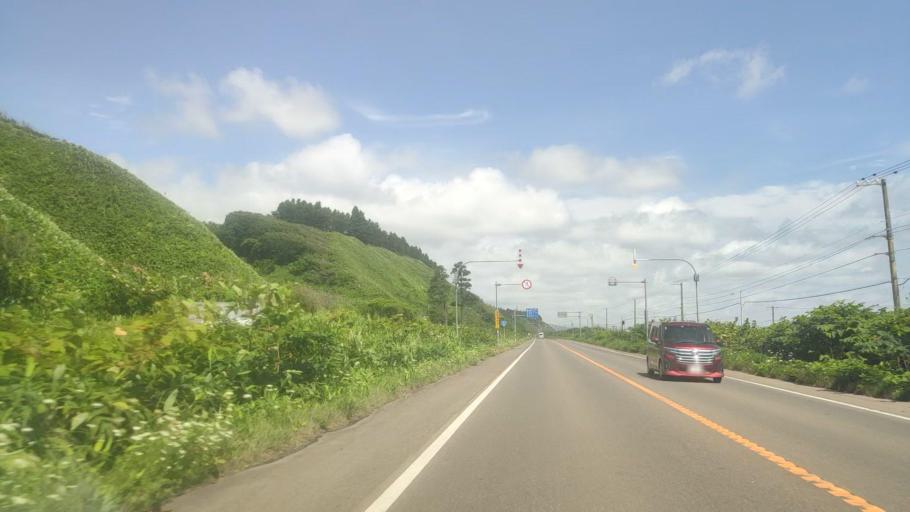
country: JP
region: Hokkaido
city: Niseko Town
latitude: 42.3480
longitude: 140.2828
